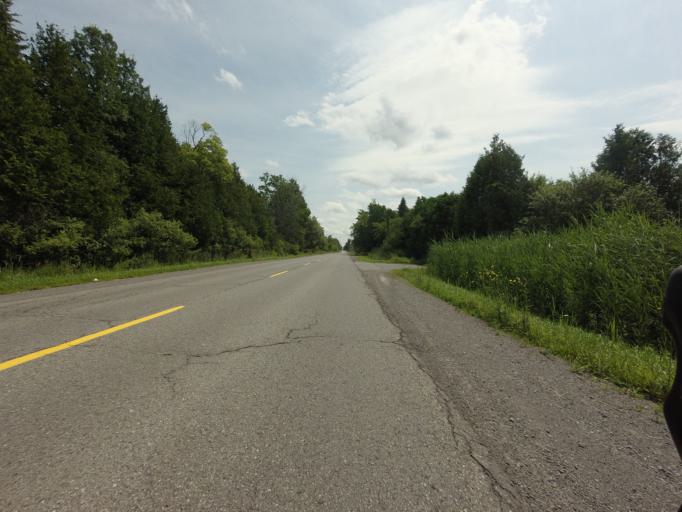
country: CA
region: Ontario
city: Ottawa
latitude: 45.2880
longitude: -75.6329
